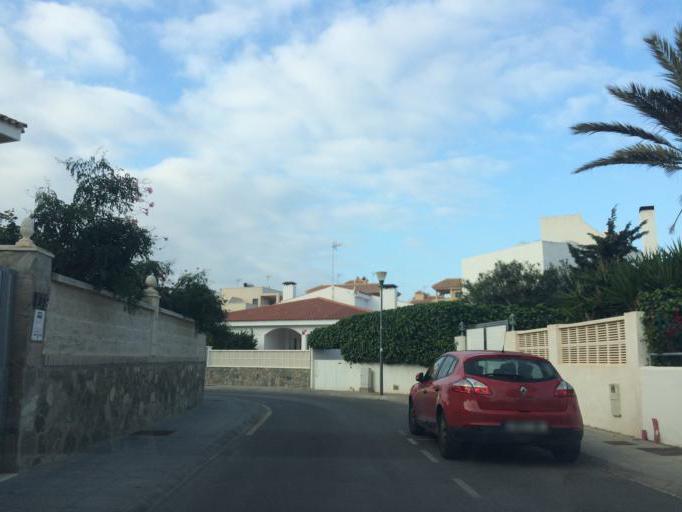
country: ES
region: Andalusia
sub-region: Provincia de Almeria
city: Almeria
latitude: 36.8248
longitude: -2.4356
